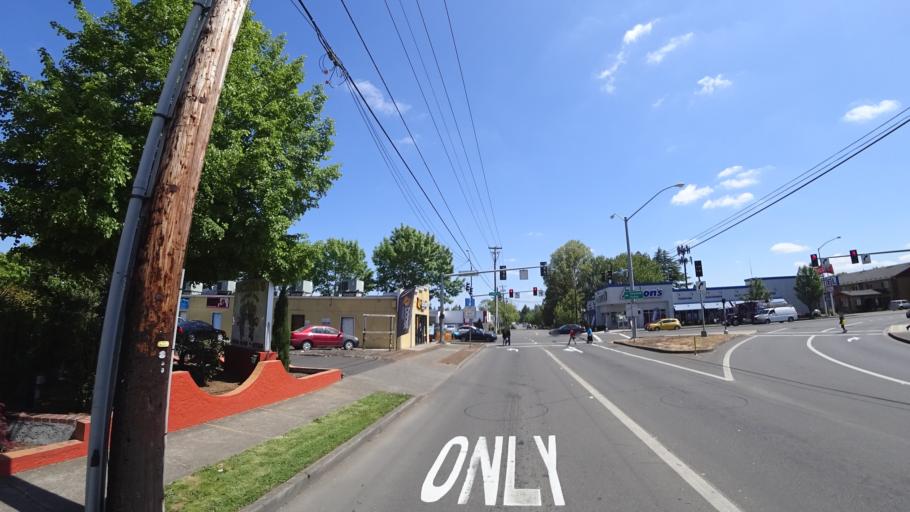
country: US
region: Oregon
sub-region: Washington County
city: Hillsboro
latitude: 45.5187
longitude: -122.9746
